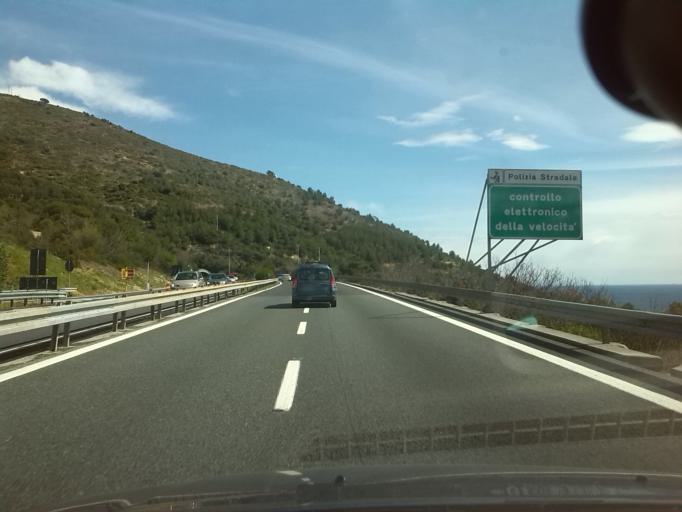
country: IT
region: Liguria
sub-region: Provincia di Savona
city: Ceriale
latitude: 44.1008
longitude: 8.2255
